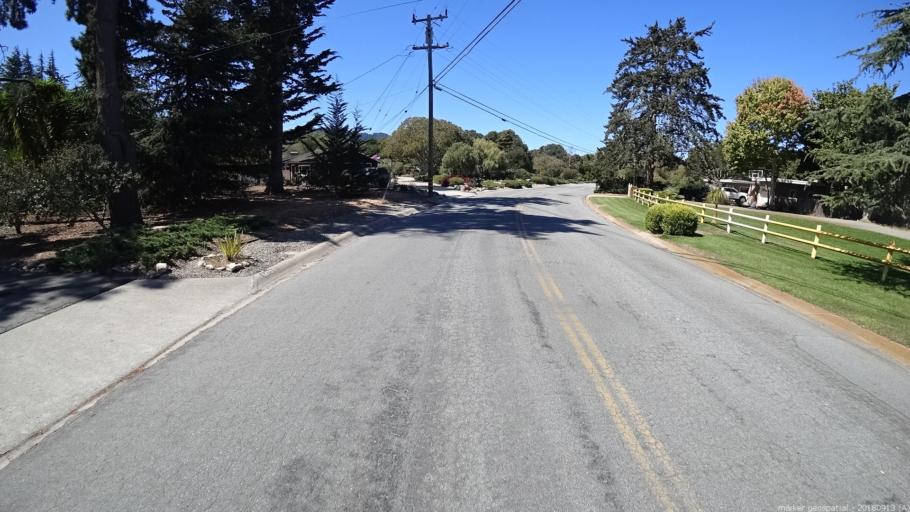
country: US
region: California
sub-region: Monterey County
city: Del Rey Oaks
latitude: 36.5350
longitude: -121.8612
